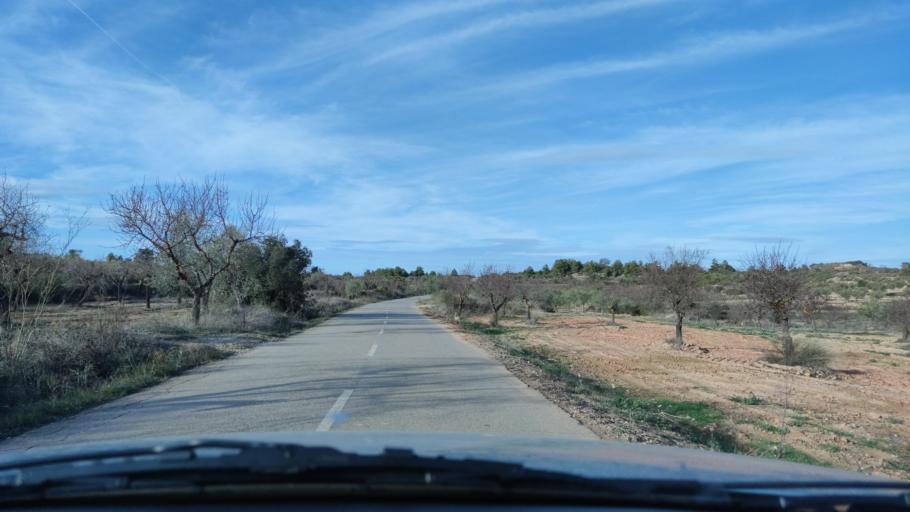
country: ES
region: Catalonia
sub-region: Provincia de Lleida
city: el Cogul
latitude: 41.4665
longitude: 0.6789
